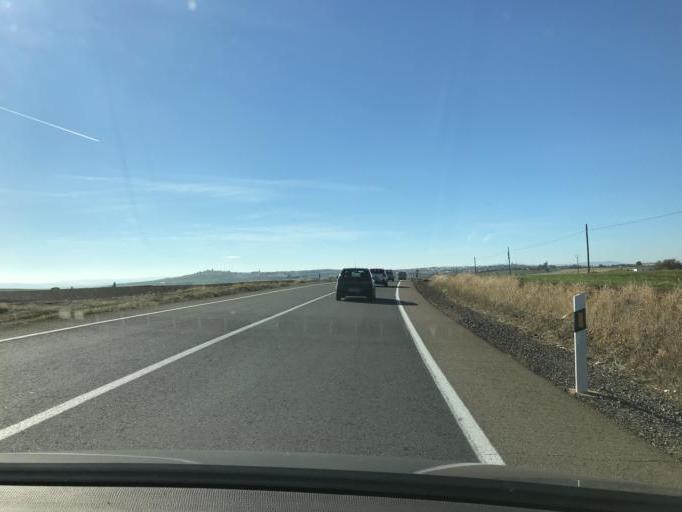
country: ES
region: Extremadura
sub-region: Provincia de Badajoz
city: Azuaga
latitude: 38.2900
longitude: -5.6553
